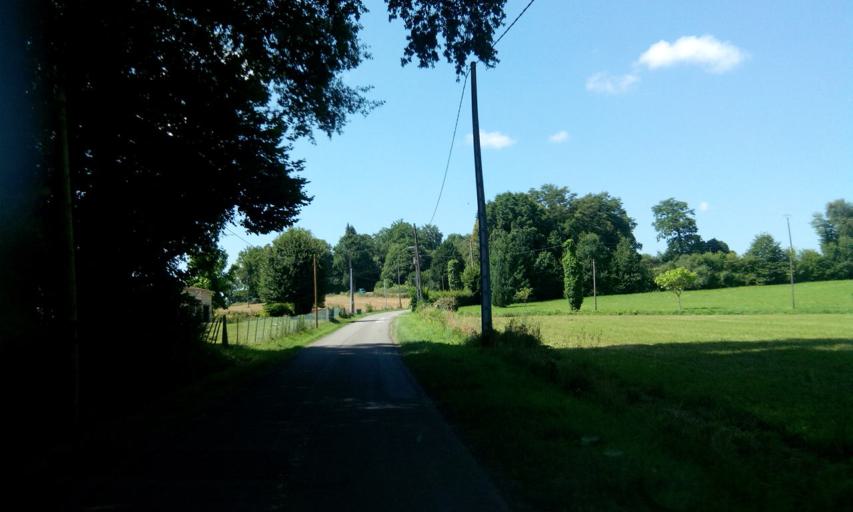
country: FR
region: Limousin
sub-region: Departement de la Haute-Vienne
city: Saint-Leonard-de-Noblat
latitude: 45.8052
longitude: 1.4618
